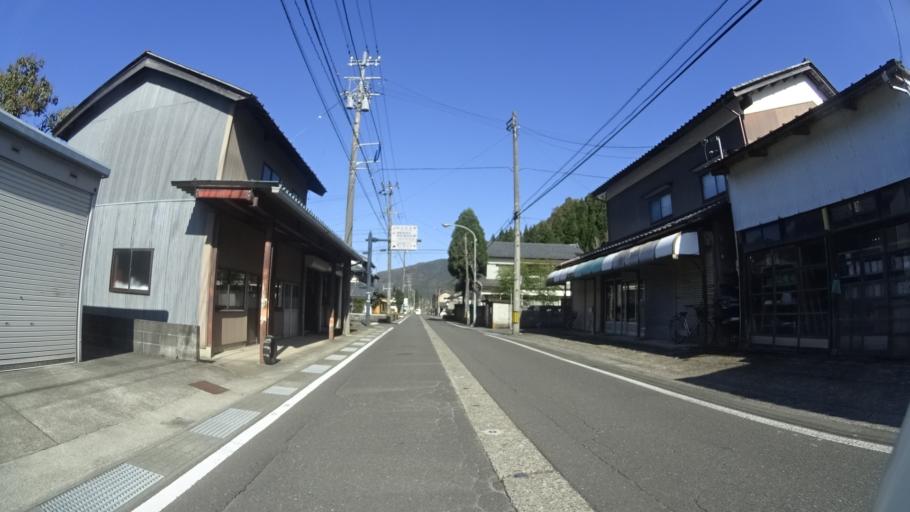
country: JP
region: Fukui
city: Ono
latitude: 35.8900
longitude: 136.3452
